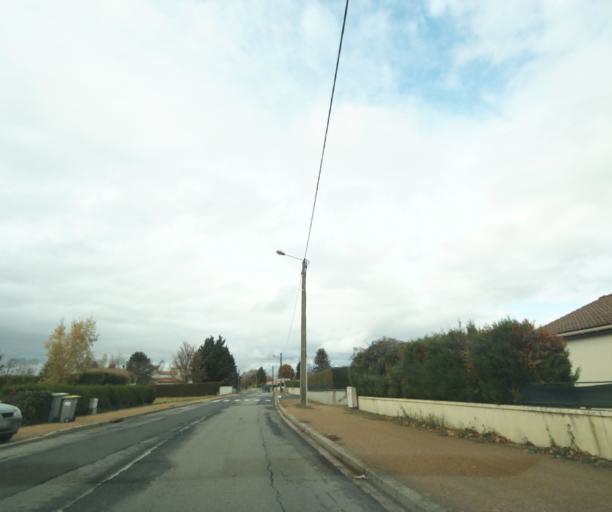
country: FR
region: Auvergne
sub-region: Departement du Puy-de-Dome
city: Pont-du-Chateau
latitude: 45.8073
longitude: 3.2434
